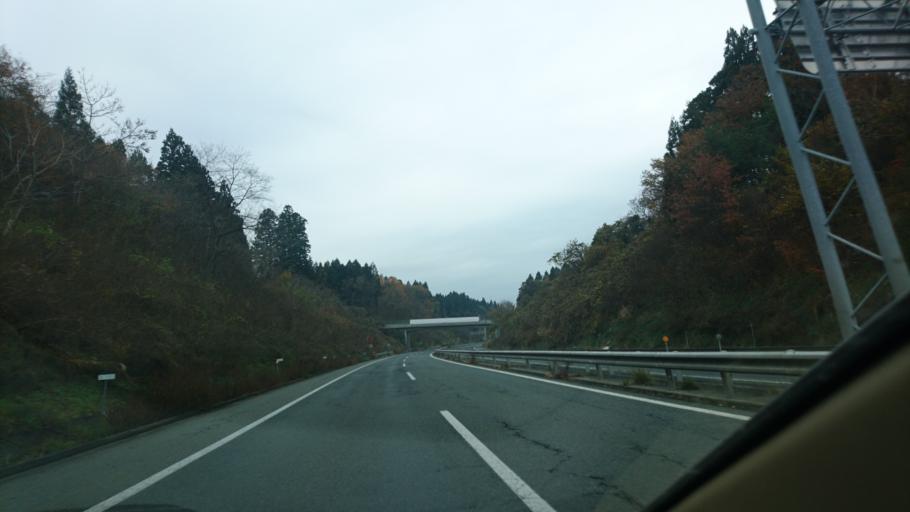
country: JP
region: Iwate
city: Kitakami
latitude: 39.2750
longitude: 141.0728
